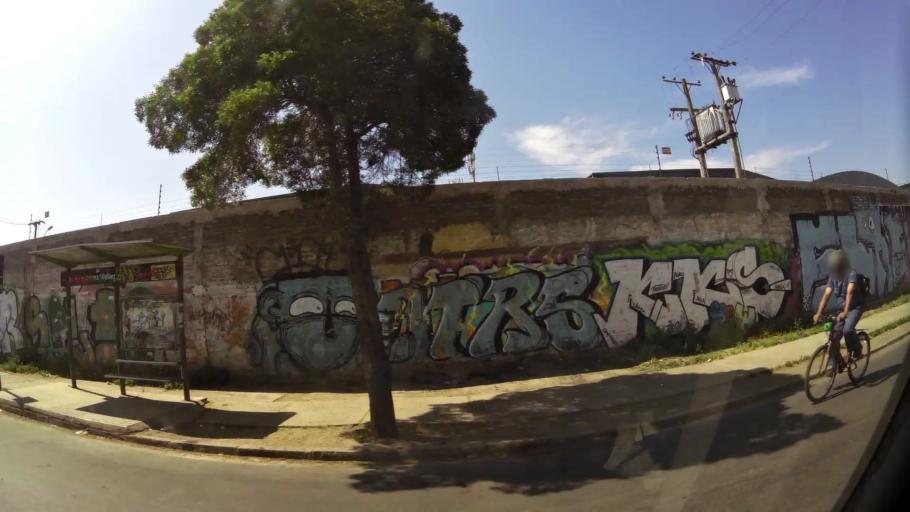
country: CL
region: Santiago Metropolitan
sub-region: Provincia de Santiago
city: Lo Prado
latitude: -33.4688
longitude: -70.7022
